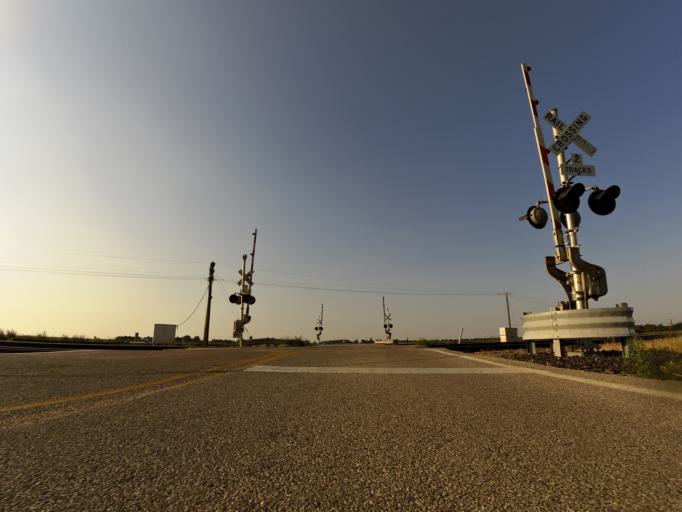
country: US
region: Kansas
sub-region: Reno County
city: South Hutchinson
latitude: 38.0078
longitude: -98.0138
